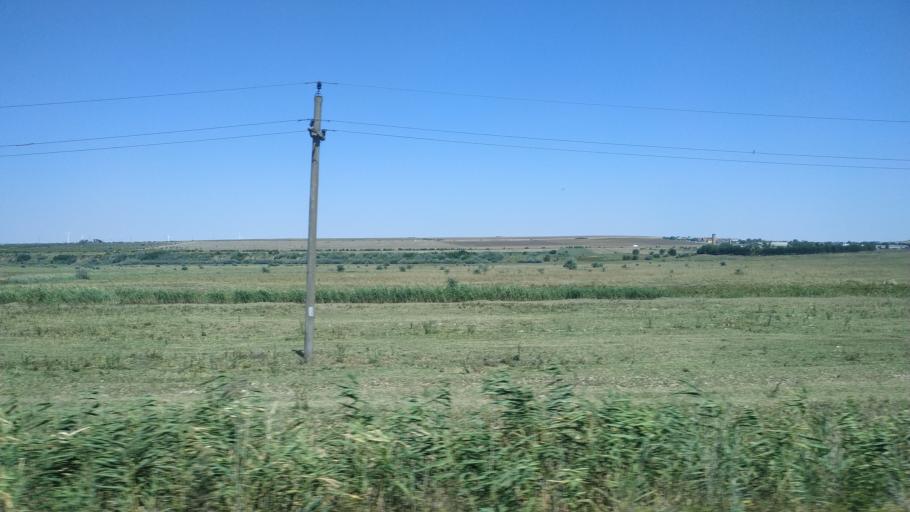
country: RO
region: Constanta
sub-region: Comuna Mircea Voda
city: Satu Nou
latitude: 44.2606
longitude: 28.2079
